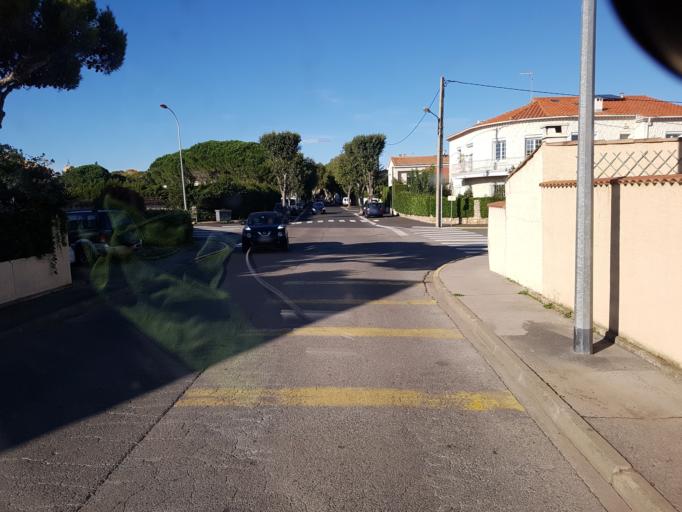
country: FR
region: Languedoc-Roussillon
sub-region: Departement de l'Aude
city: Narbonne
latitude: 43.1756
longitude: 3.0036
